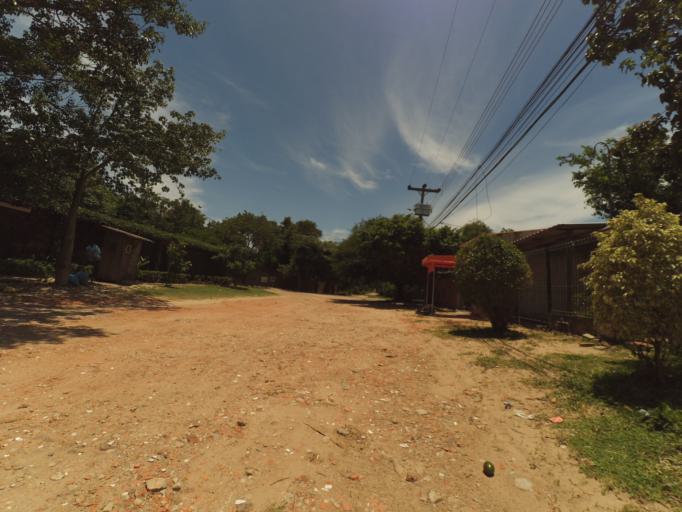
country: BO
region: Santa Cruz
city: Santa Cruz de la Sierra
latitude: -17.8099
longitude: -63.2286
